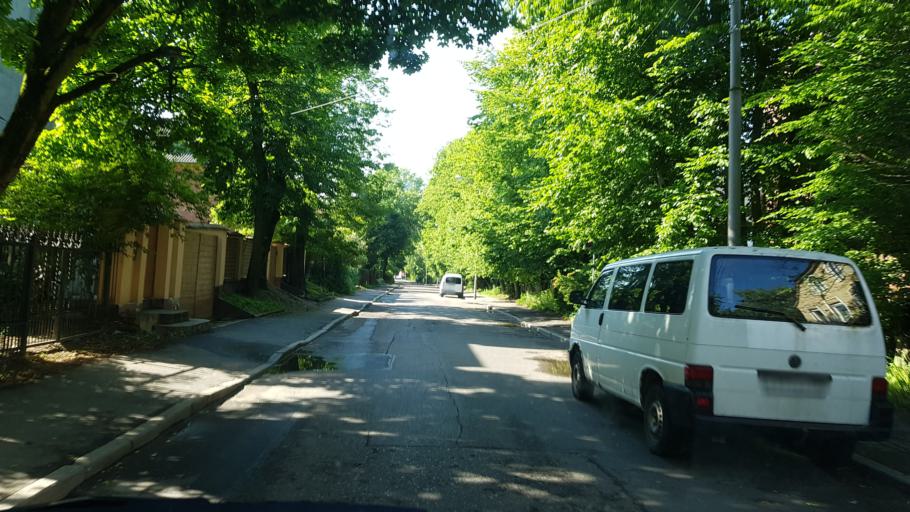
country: RU
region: Kaliningrad
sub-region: Gorod Kaliningrad
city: Kaliningrad
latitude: 54.7169
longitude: 20.4569
